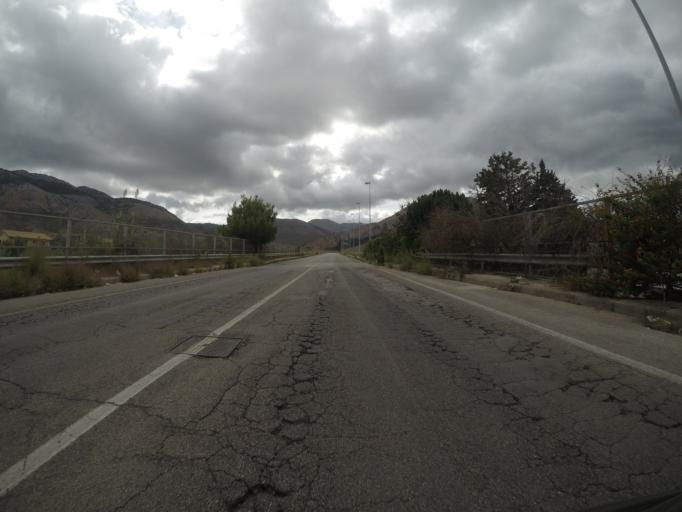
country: IT
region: Sicily
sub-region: Palermo
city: Capaci
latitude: 38.1698
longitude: 13.2209
